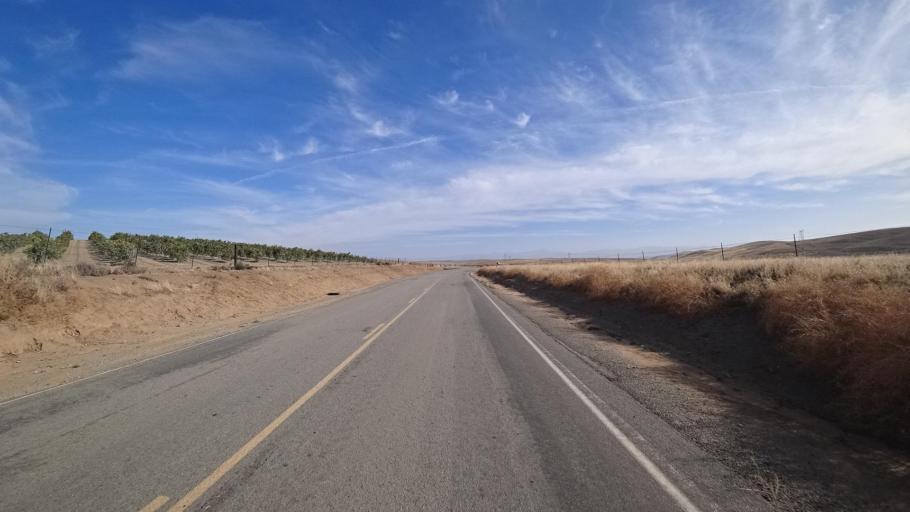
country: US
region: California
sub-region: Tulare County
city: Richgrove
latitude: 35.6180
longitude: -119.0472
